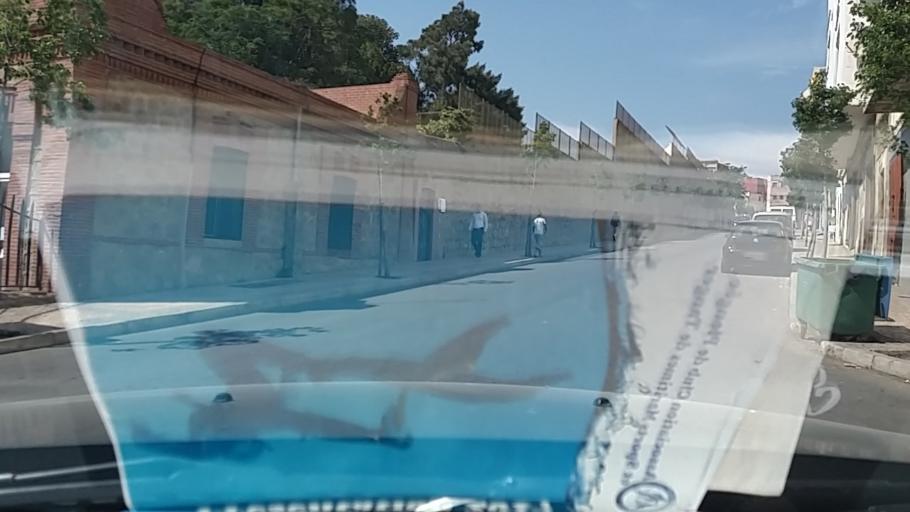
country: MA
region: Tanger-Tetouan
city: Tetouan
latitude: 35.5724
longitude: -5.3876
